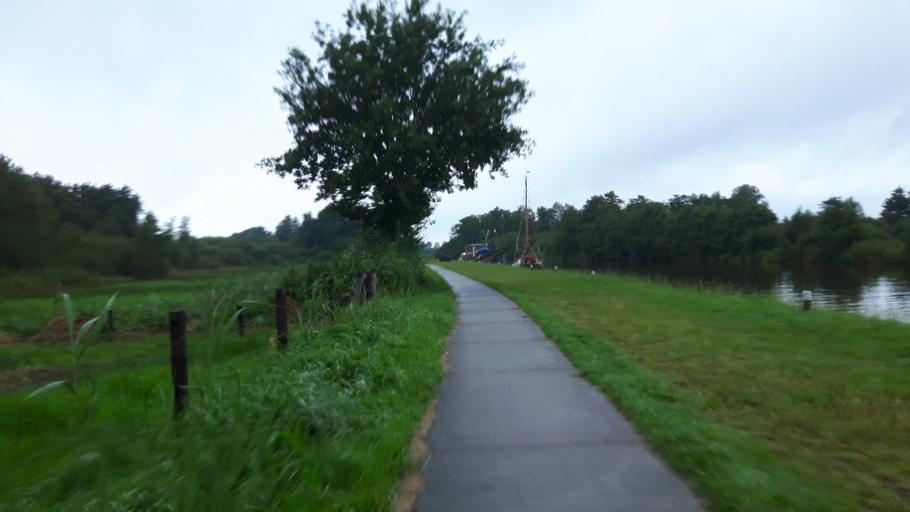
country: NL
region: Overijssel
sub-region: Gemeente Steenwijkerland
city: Oldemarkt
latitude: 52.7963
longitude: 5.9985
